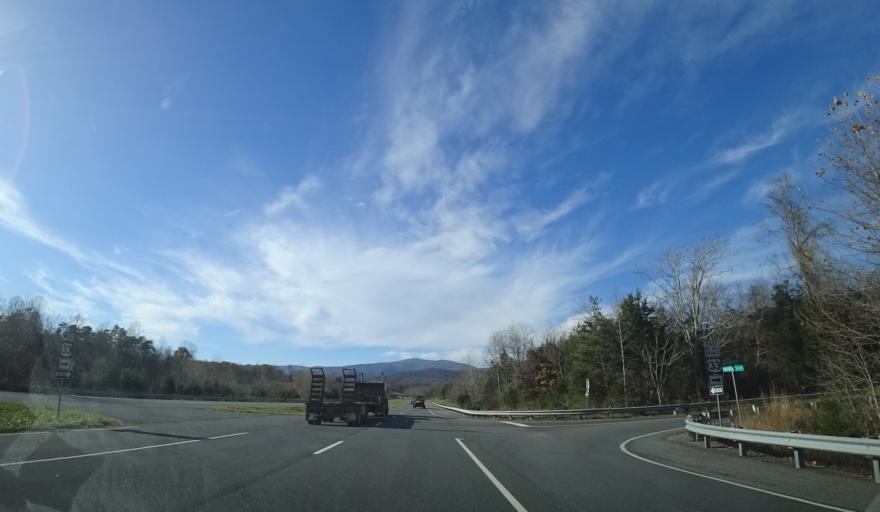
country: US
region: Virginia
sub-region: Greene County
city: Stanardsville
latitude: 38.2953
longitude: -78.4510
